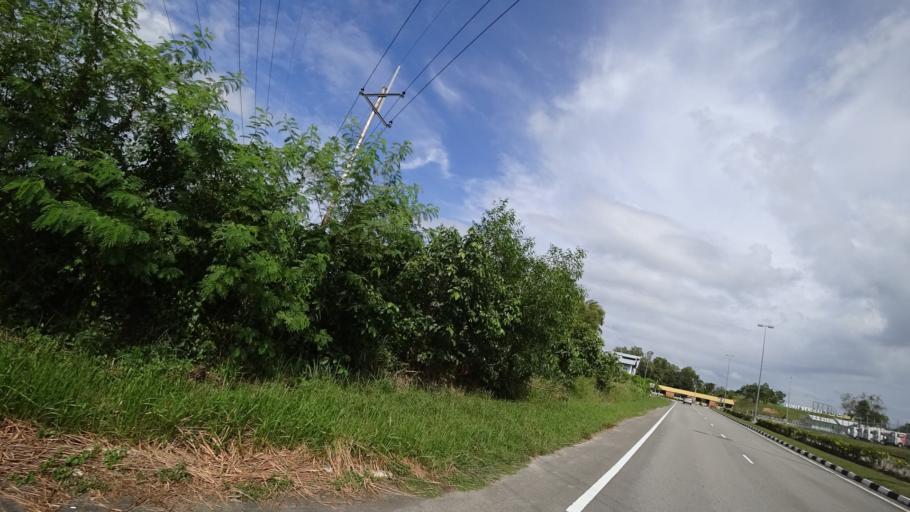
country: BN
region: Tutong
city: Tutong
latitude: 4.8092
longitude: 114.6590
